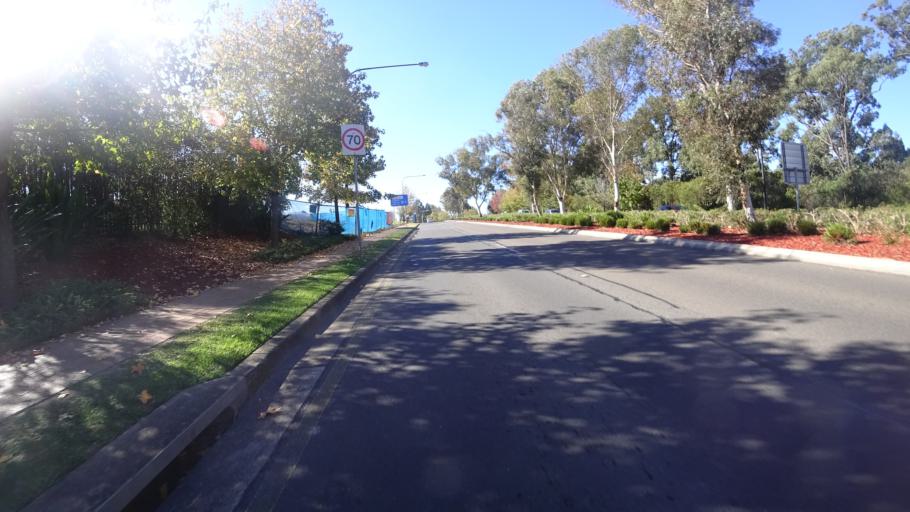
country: AU
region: New South Wales
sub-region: Blacktown
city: Stanhope Gardens
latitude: -33.7397
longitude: 150.9485
